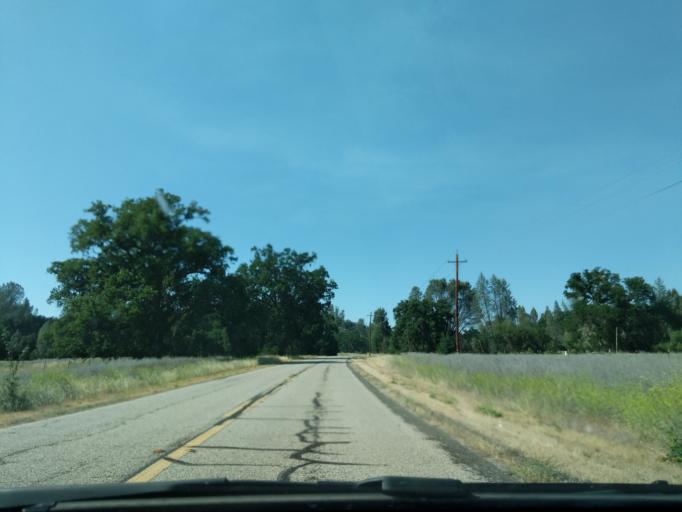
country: US
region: California
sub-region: Monterey County
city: King City
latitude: 35.9917
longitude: -121.1796
